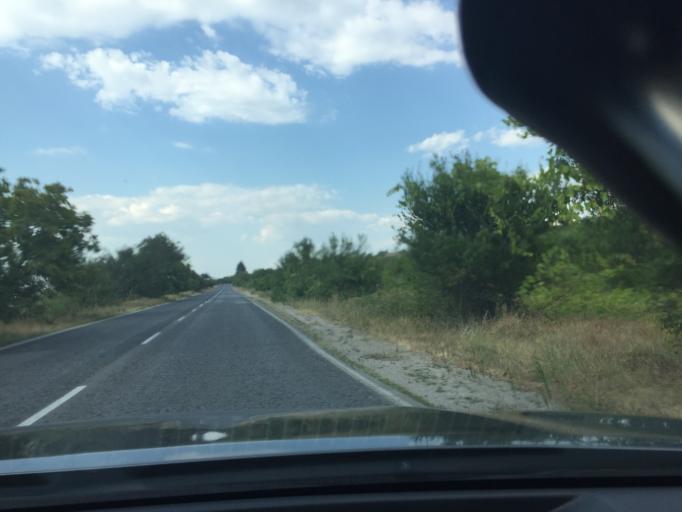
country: BG
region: Kyustendil
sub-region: Obshtina Boboshevo
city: Boboshevo
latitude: 42.1382
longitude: 23.0398
